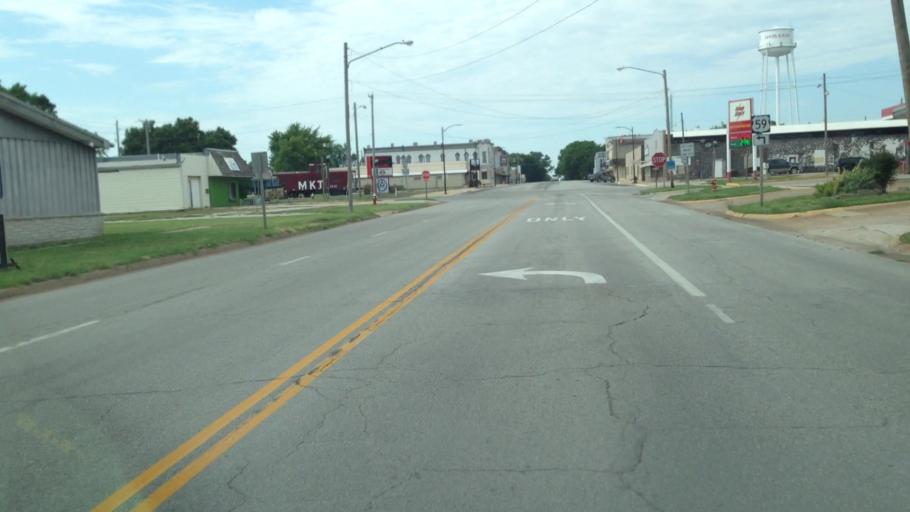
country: US
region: Kansas
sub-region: Labette County
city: Oswego
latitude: 37.1640
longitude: -95.1088
